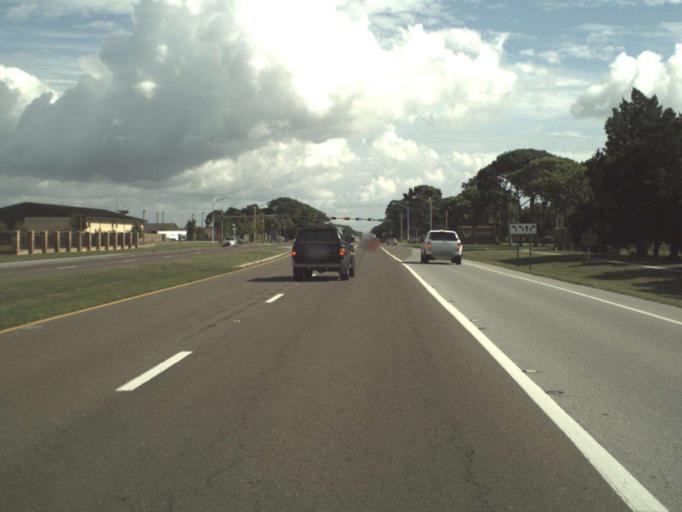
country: US
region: Florida
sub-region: Bay County
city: Tyndall Air Force Base
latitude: 30.0717
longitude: -85.5926
